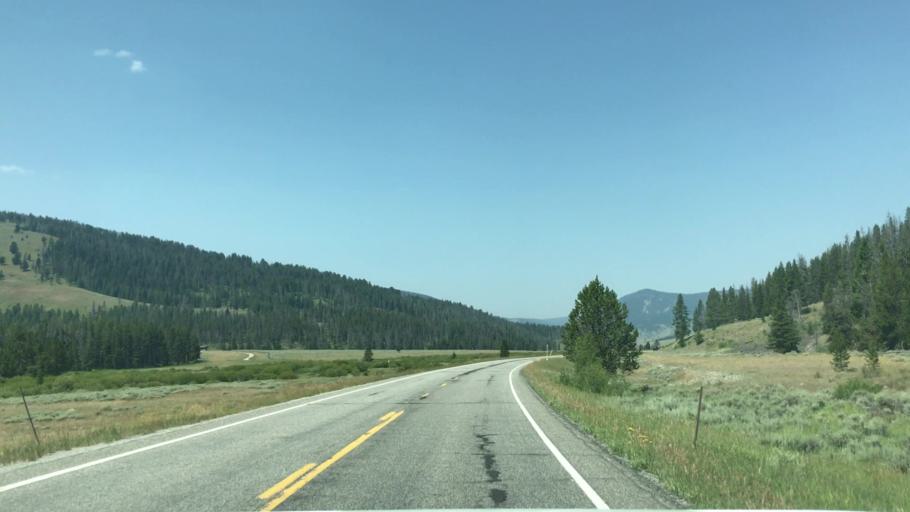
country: US
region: Montana
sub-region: Gallatin County
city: West Yellowstone
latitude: 45.0273
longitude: -111.1054
